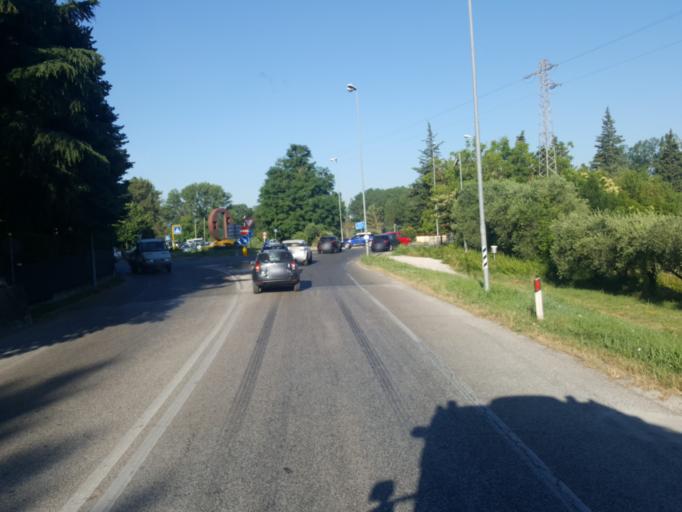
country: IT
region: The Marches
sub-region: Provincia di Pesaro e Urbino
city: Montelabbate
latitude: 43.8513
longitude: 12.7886
